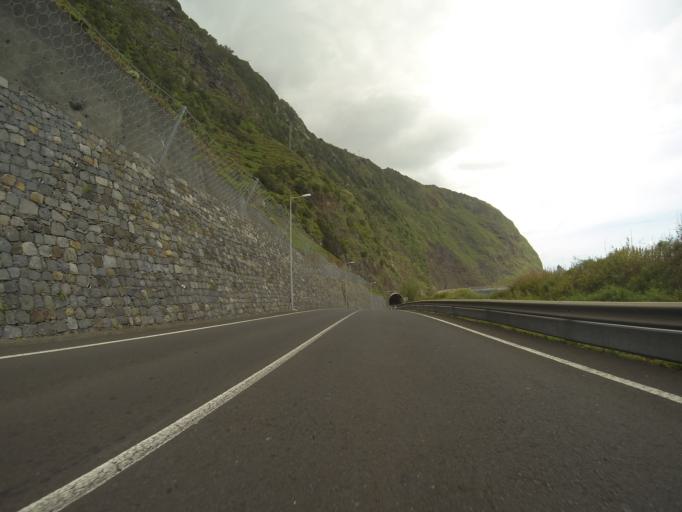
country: PT
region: Madeira
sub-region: Porto Moniz
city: Porto Moniz
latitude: 32.8476
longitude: -17.1493
